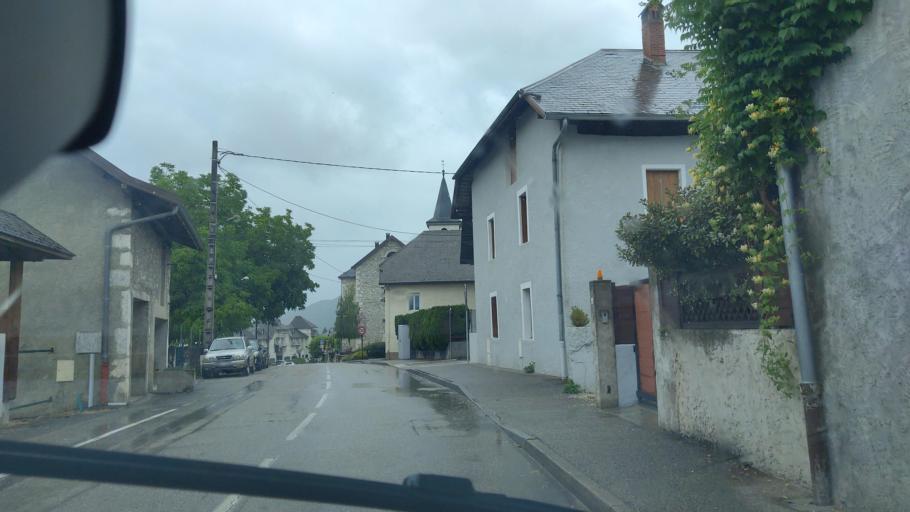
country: FR
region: Rhone-Alpes
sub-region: Departement de la Savoie
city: La Biolle
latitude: 45.7569
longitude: 5.9288
